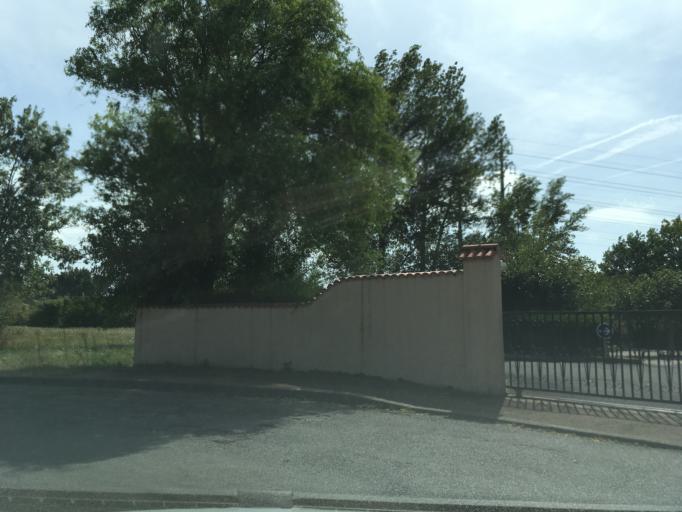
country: FR
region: Midi-Pyrenees
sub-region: Departement du Tarn
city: Castres
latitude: 43.6224
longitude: 2.2654
